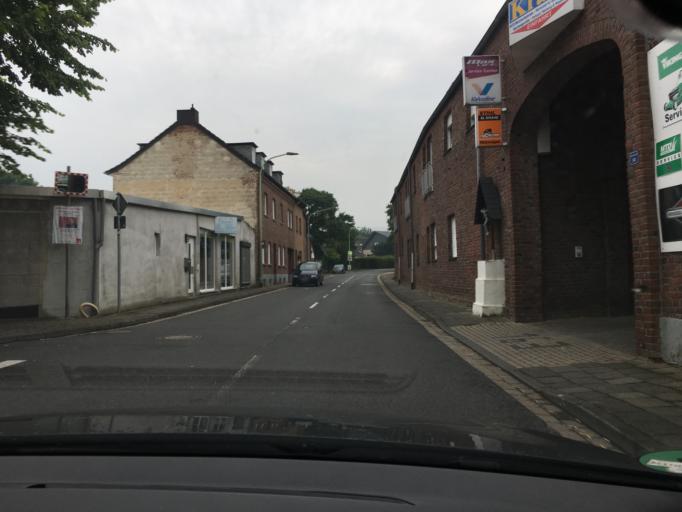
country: DE
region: North Rhine-Westphalia
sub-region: Regierungsbezirk Koln
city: Niederzier
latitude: 50.9014
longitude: 6.4446
